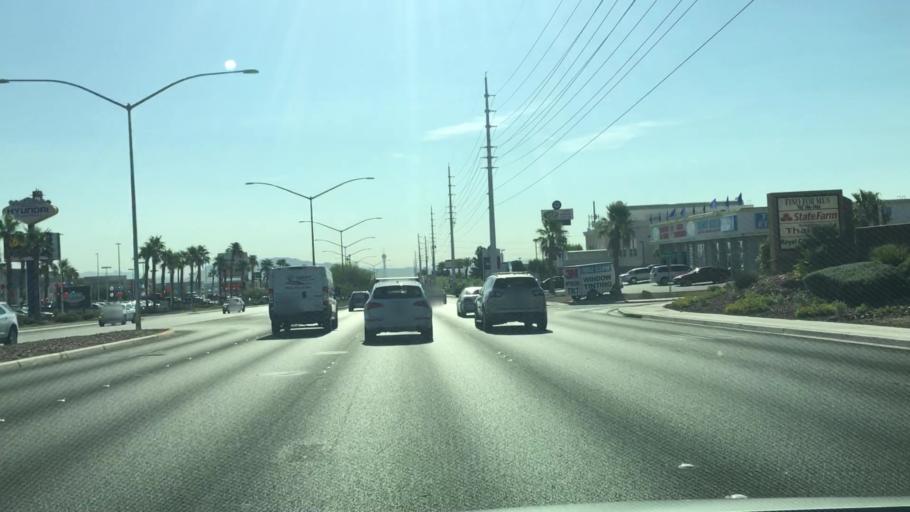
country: US
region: Nevada
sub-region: Clark County
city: Spring Valley
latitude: 36.1439
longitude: -115.2502
